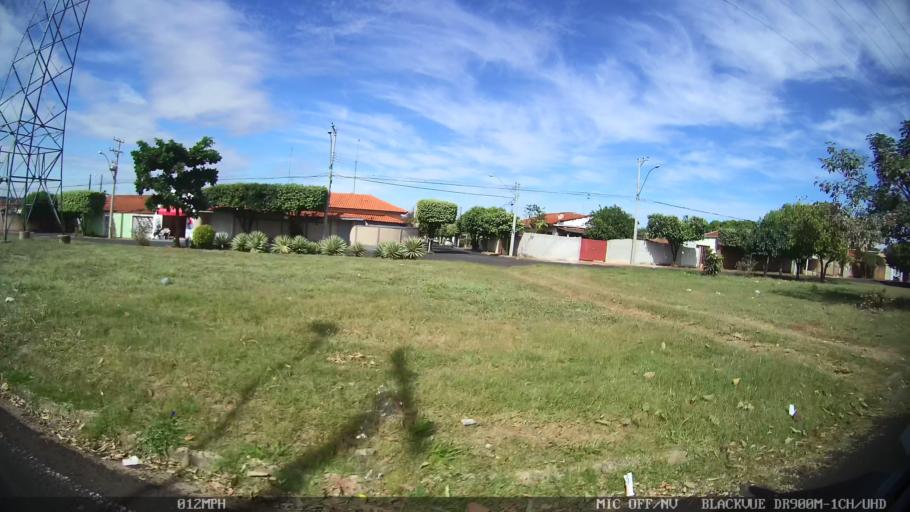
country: BR
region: Sao Paulo
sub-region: Sao Jose Do Rio Preto
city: Sao Jose do Rio Preto
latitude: -20.8350
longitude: -49.3522
